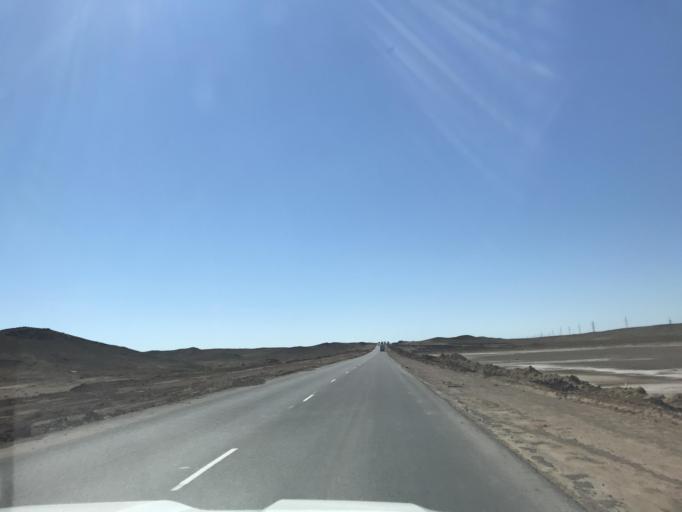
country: KZ
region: Zhambyl
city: Mynaral
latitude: 45.3094
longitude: 73.7534
